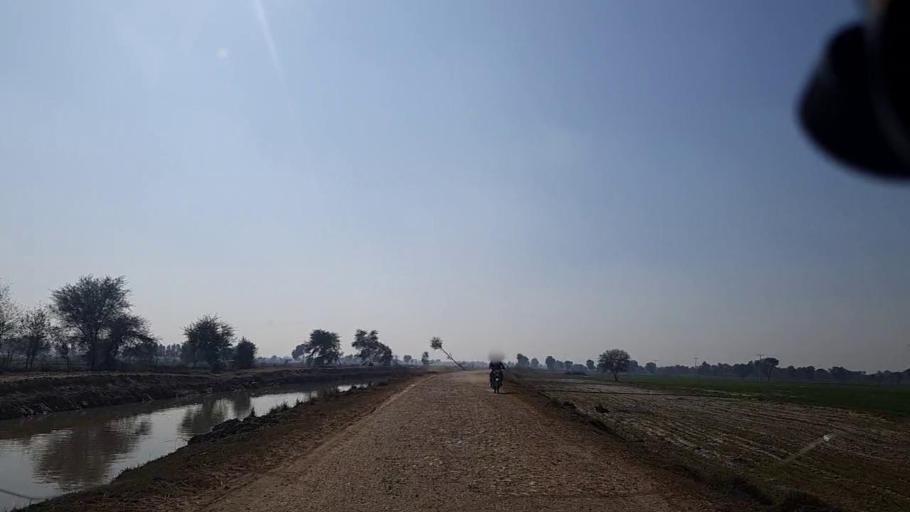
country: PK
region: Sindh
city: Khanpur
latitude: 27.8004
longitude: 69.4093
